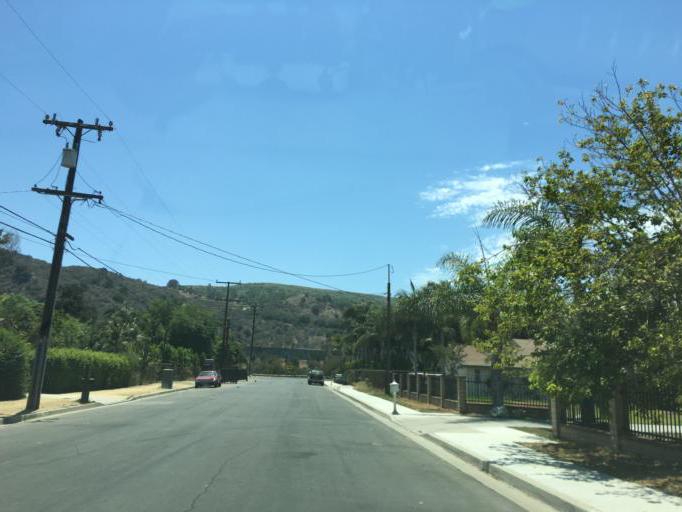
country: US
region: California
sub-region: Los Angeles County
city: Avocado Heights
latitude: 34.0310
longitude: -117.9964
